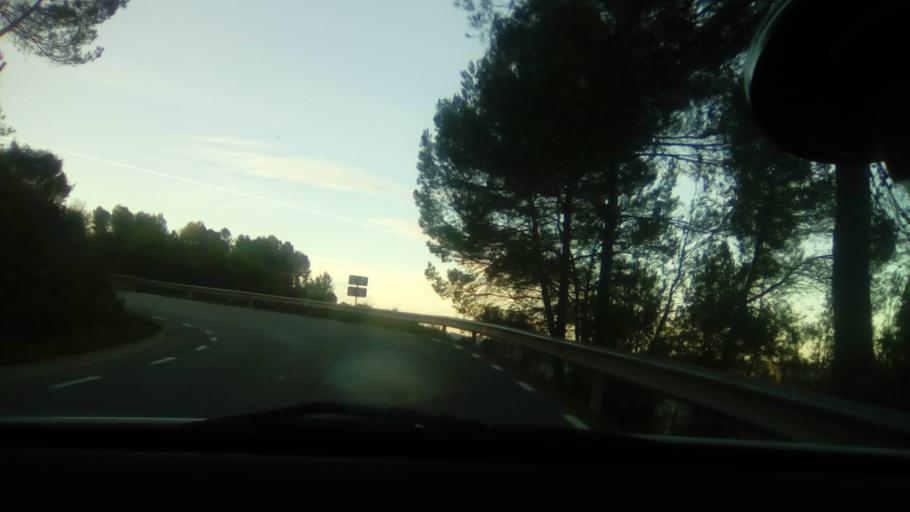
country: ES
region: Catalonia
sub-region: Provincia de Barcelona
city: Navarcles
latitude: 41.7462
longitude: 1.9064
